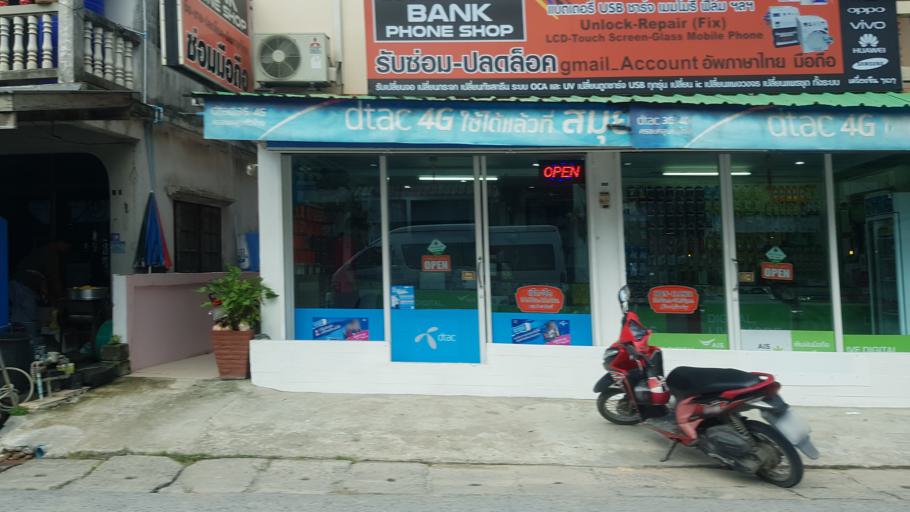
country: TH
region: Surat Thani
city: Ko Samui
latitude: 9.5293
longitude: 100.0448
